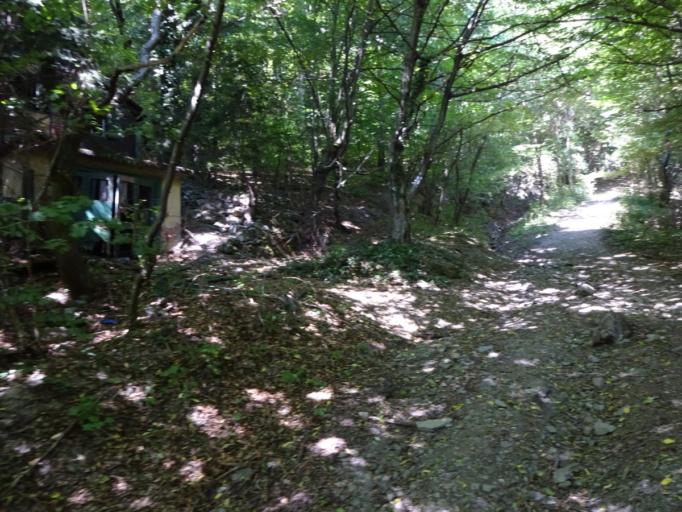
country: AT
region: Burgenland
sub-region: Politischer Bezirk Oberwart
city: Rechnitz
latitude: 47.3523
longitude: 16.4829
